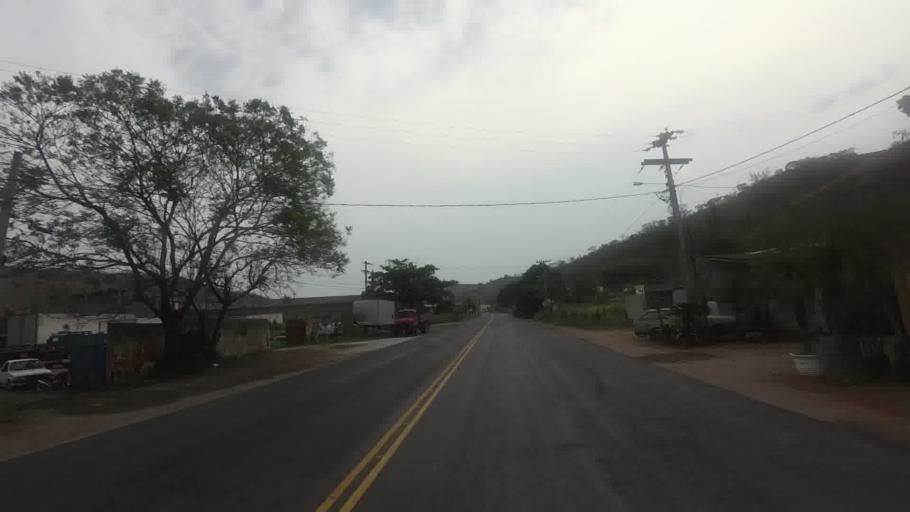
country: BR
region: Rio de Janeiro
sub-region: Santo Antonio De Padua
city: Santo Antonio de Padua
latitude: -21.5349
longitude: -42.1545
